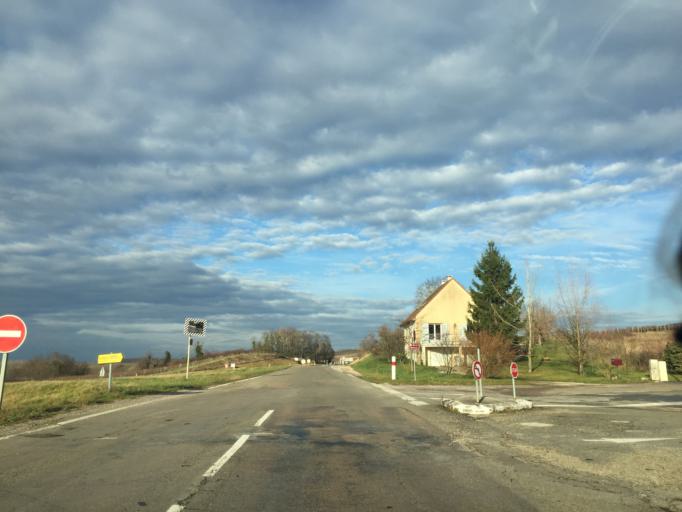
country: FR
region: Franche-Comte
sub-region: Departement du Jura
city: Arbois
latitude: 46.9128
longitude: 5.7704
